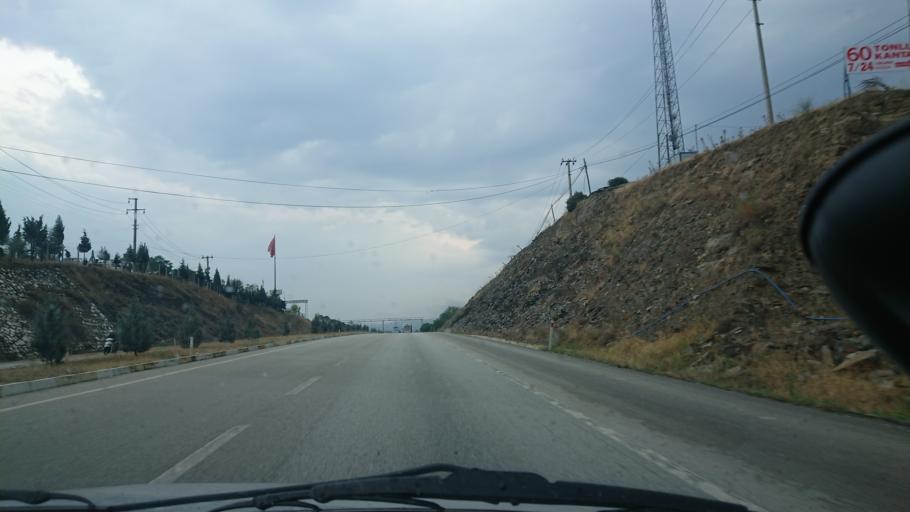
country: TR
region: Manisa
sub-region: Kula
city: Kula
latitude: 38.5481
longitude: 28.6724
